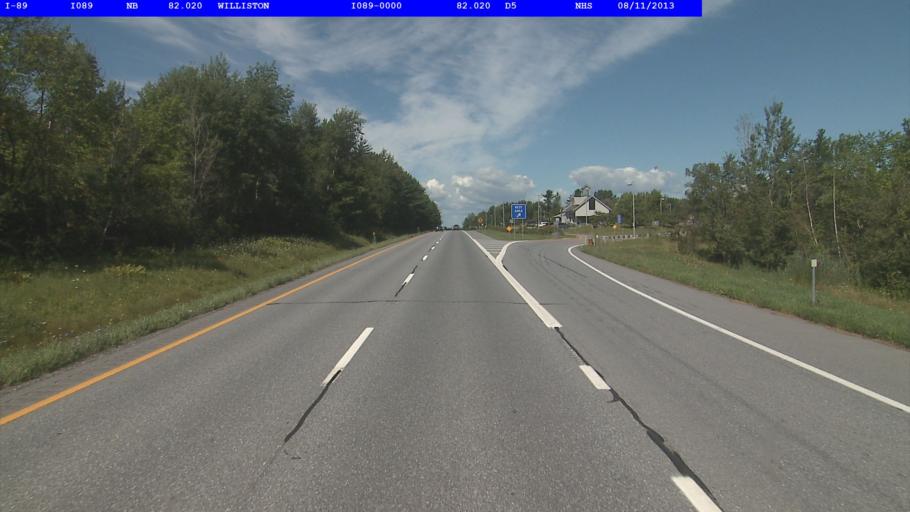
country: US
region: Vermont
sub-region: Chittenden County
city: Williston
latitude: 44.4354
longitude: -73.0763
